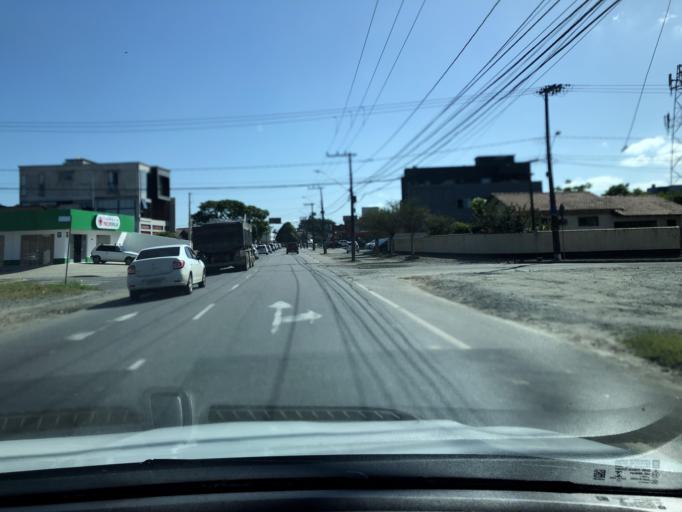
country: BR
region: Santa Catarina
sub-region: Joinville
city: Joinville
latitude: -26.3198
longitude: -48.8313
